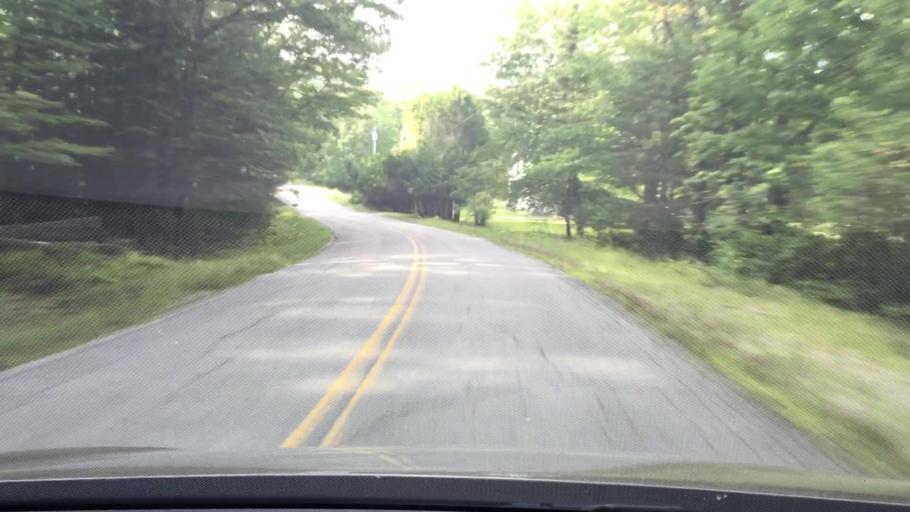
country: US
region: Maine
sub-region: Hancock County
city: Orland
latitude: 44.5312
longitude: -68.7638
